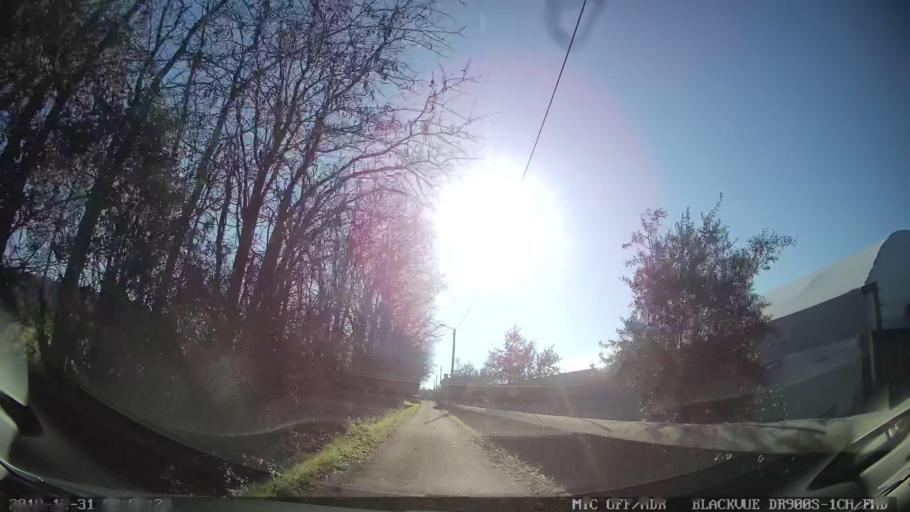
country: PT
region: Castelo Branco
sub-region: Idanha-A-Nova
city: Idanha-a-Nova
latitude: 39.9141
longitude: -7.2193
